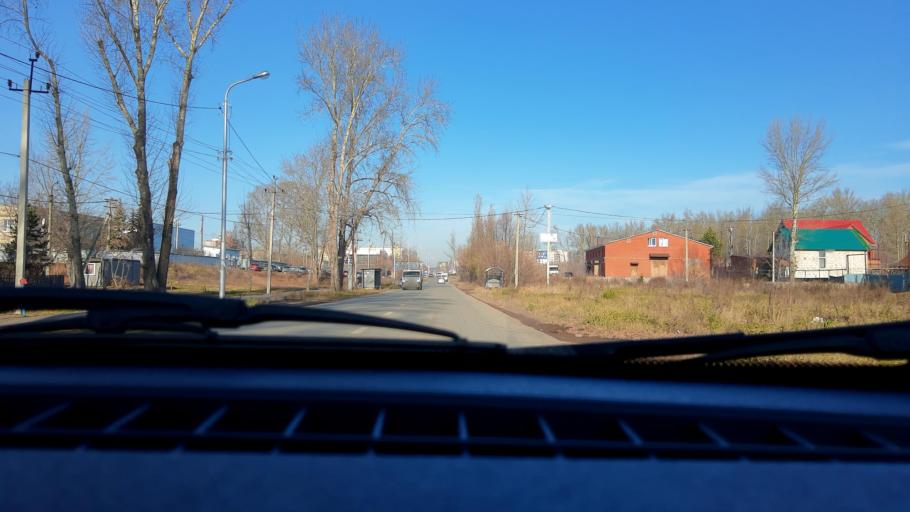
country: RU
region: Bashkortostan
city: Mikhaylovka
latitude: 54.7733
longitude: 55.8934
